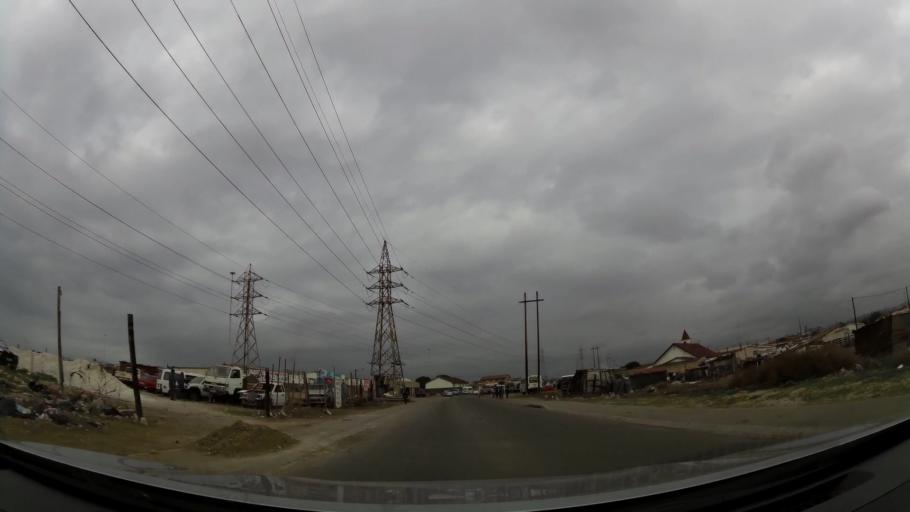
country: ZA
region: Eastern Cape
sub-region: Nelson Mandela Bay Metropolitan Municipality
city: Port Elizabeth
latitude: -33.8832
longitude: 25.5838
